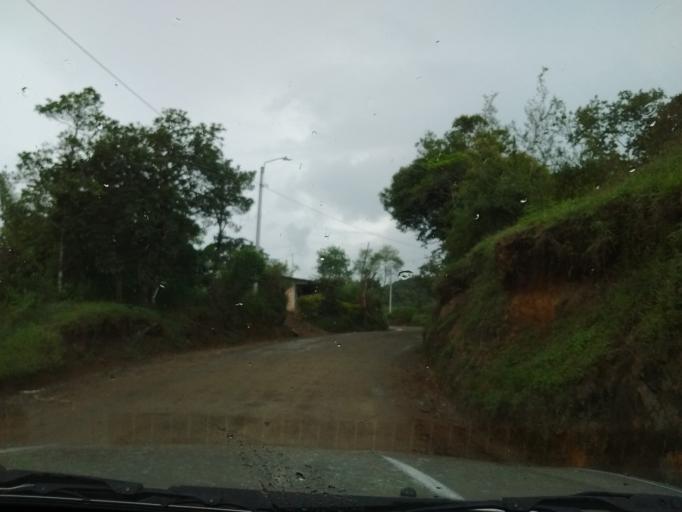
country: CO
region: Cauca
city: Popayan
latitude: 2.5211
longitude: -76.5926
